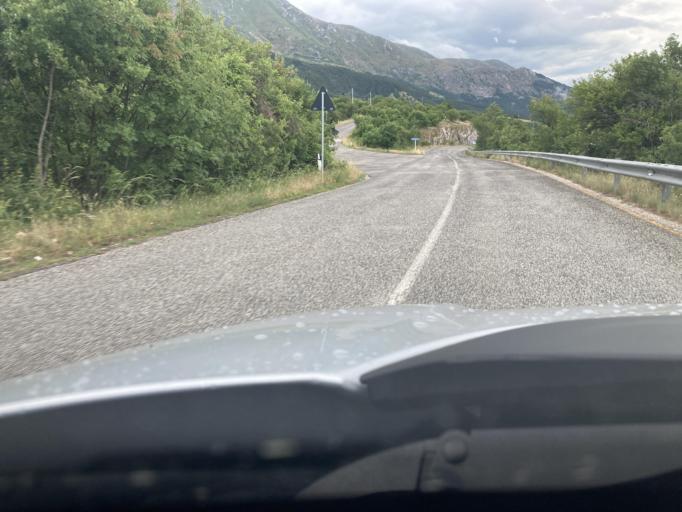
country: IT
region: Abruzzo
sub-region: Provincia dell' Aquila
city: San Panfilo d'Ocre
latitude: 42.2739
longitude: 13.4845
